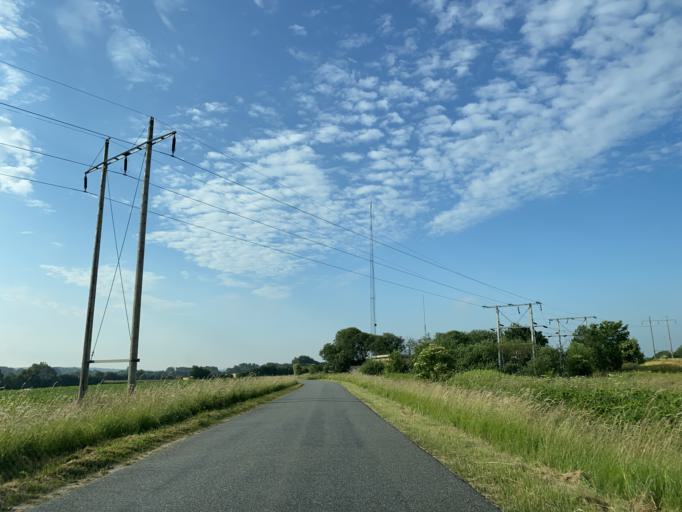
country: DK
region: South Denmark
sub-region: Haderslev Kommune
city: Haderslev
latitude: 55.1905
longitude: 9.4712
